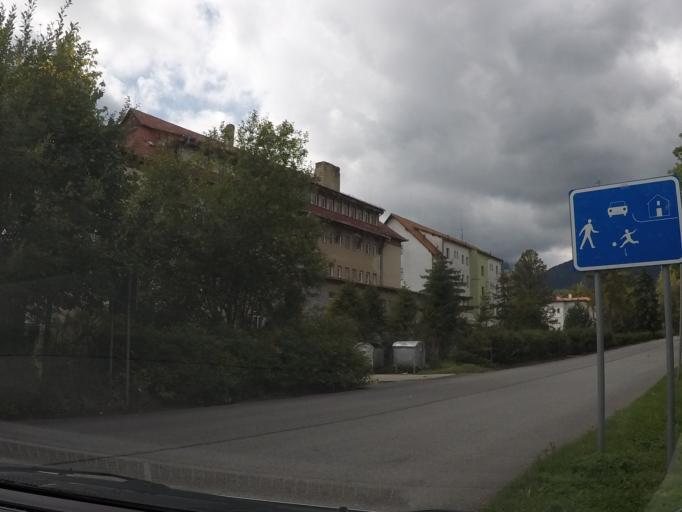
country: SK
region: Presovsky
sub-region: Okres Poprad
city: Nova Lesna
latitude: 49.1615
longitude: 20.2877
